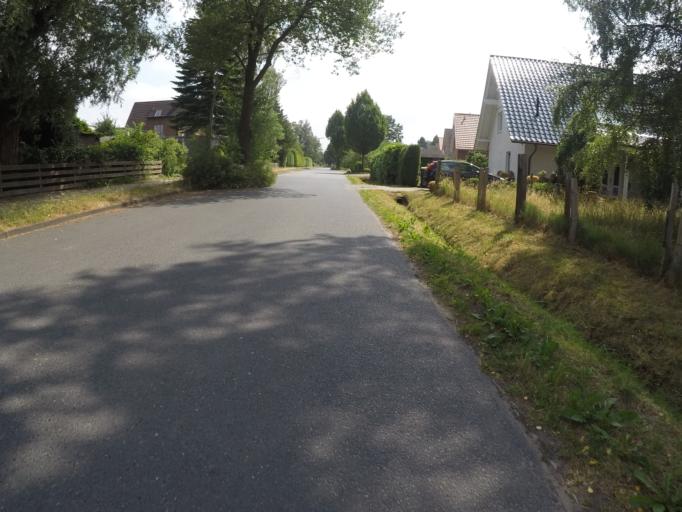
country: DE
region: Hamburg
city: Sasel
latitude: 53.6372
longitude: 10.1239
